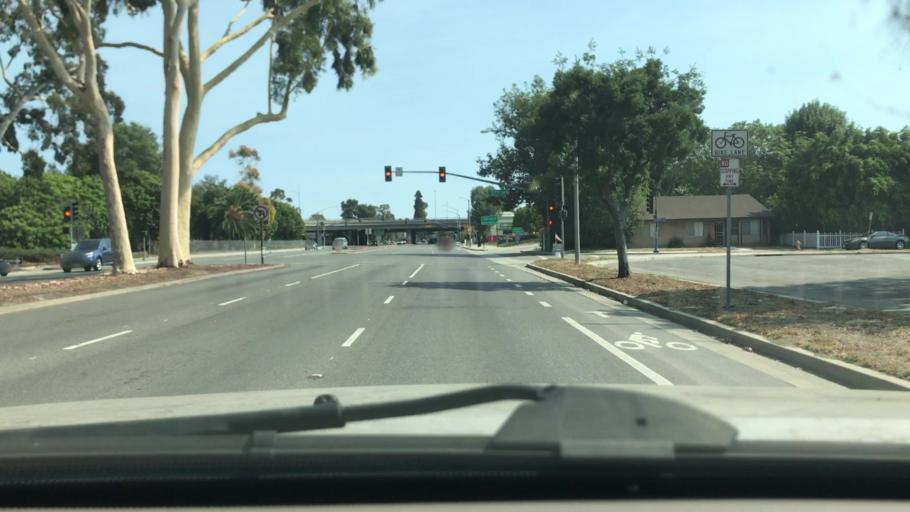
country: US
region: California
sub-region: Los Angeles County
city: Signal Hill
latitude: 33.8055
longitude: -118.1254
